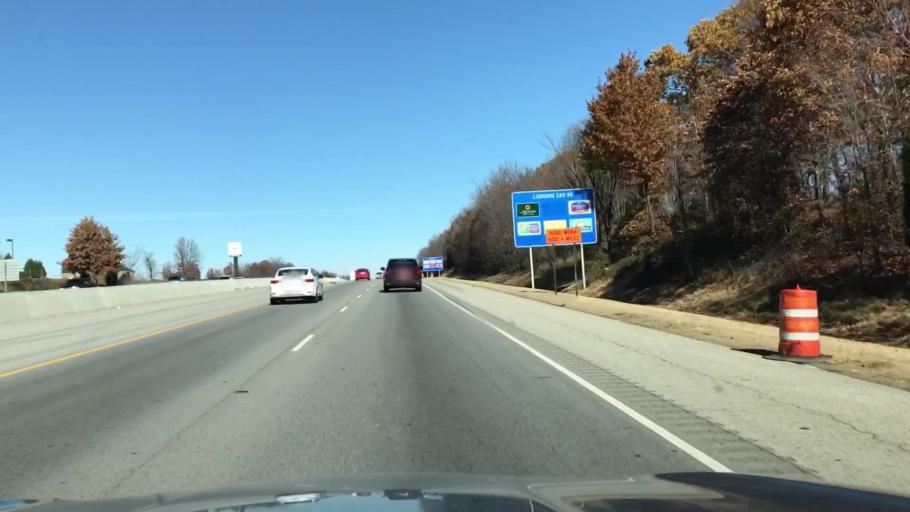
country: US
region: Arkansas
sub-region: Benton County
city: Bentonville
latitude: 36.3239
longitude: -94.1847
